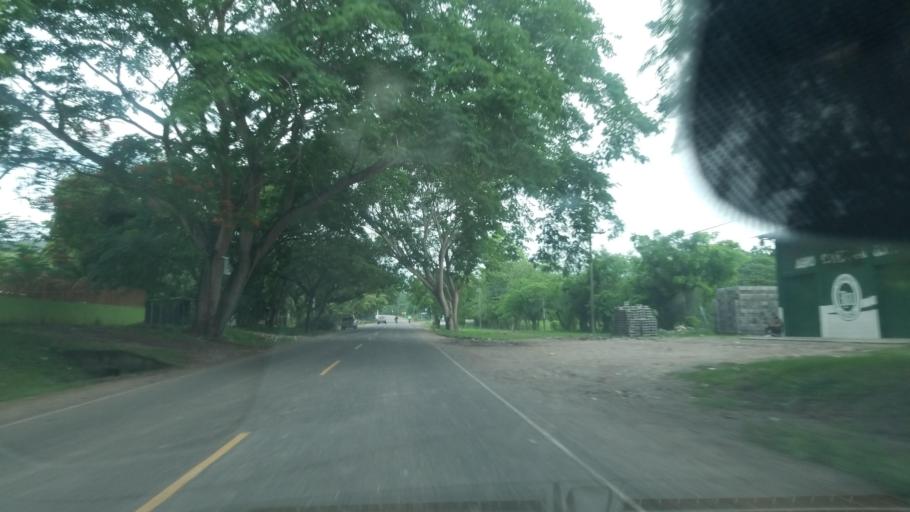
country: HN
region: Santa Barbara
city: San Vicente Centenario
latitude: 14.8823
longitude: -88.2486
